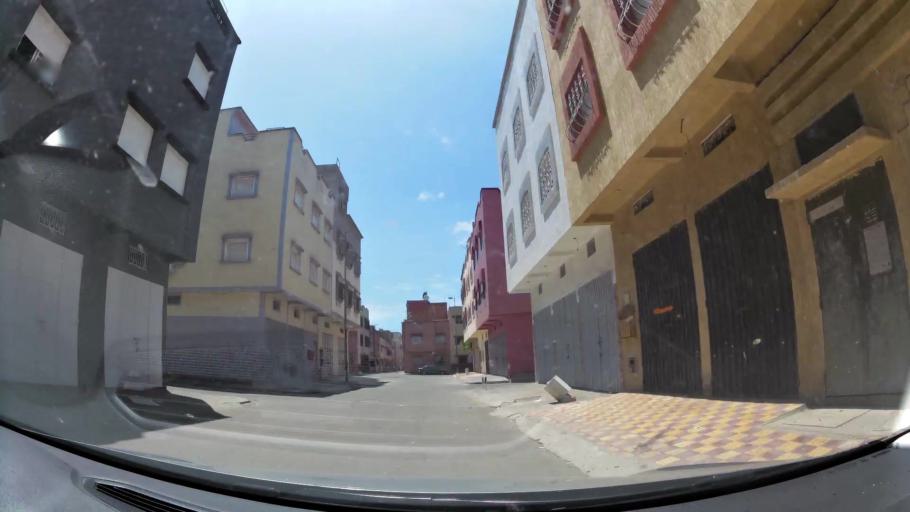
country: MA
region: Gharb-Chrarda-Beni Hssen
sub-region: Kenitra Province
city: Kenitra
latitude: 34.2649
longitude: -6.5536
